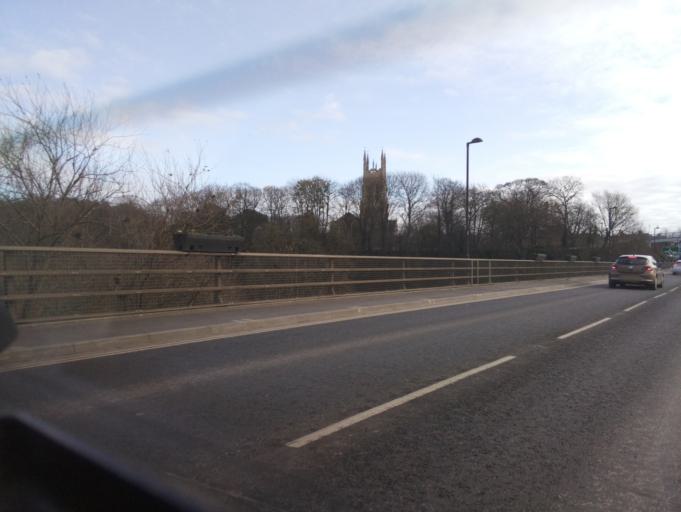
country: GB
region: England
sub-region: Staffordshire
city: Burton upon Trent
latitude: 52.7956
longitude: -1.6256
